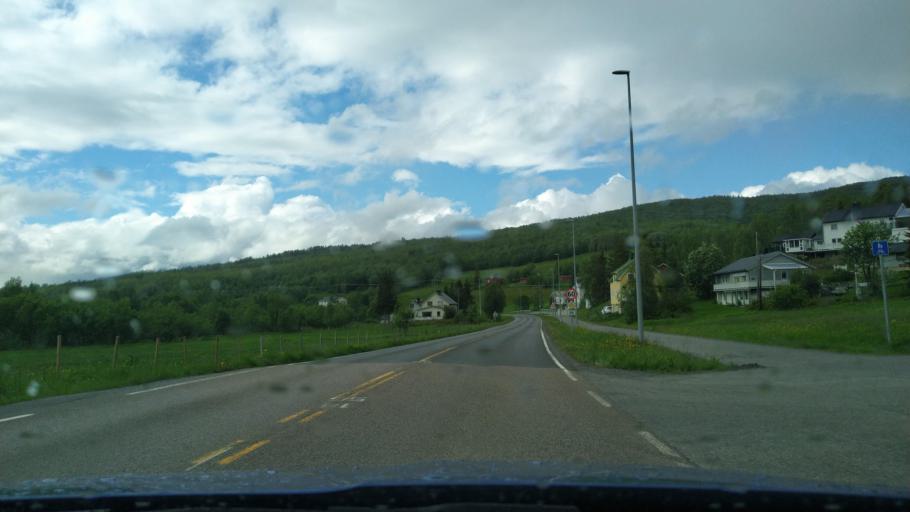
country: NO
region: Troms
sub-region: Sorreisa
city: Sorreisa
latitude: 69.1701
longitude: 18.1148
